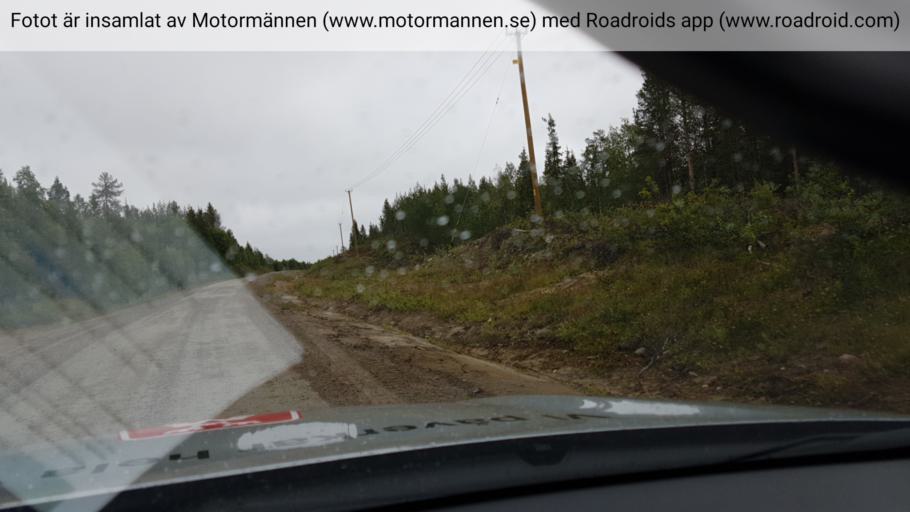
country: SE
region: Norrbotten
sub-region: Gallivare Kommun
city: Gaellivare
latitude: 66.7149
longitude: 20.4897
